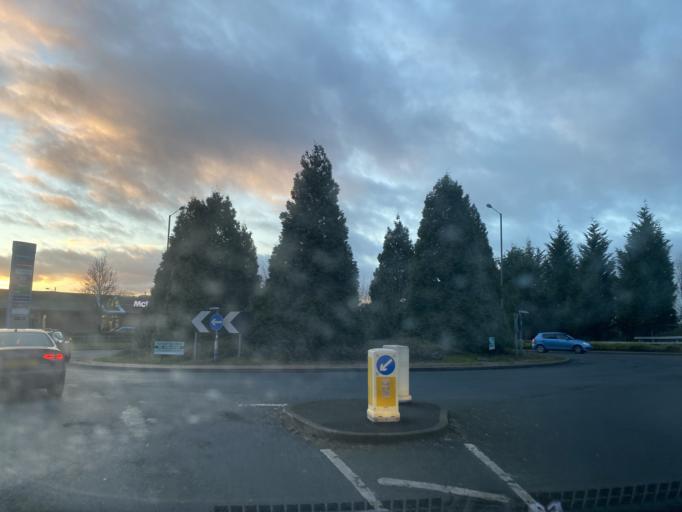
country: GB
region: England
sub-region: Walsall
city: Walsall
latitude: 52.5968
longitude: -1.9997
